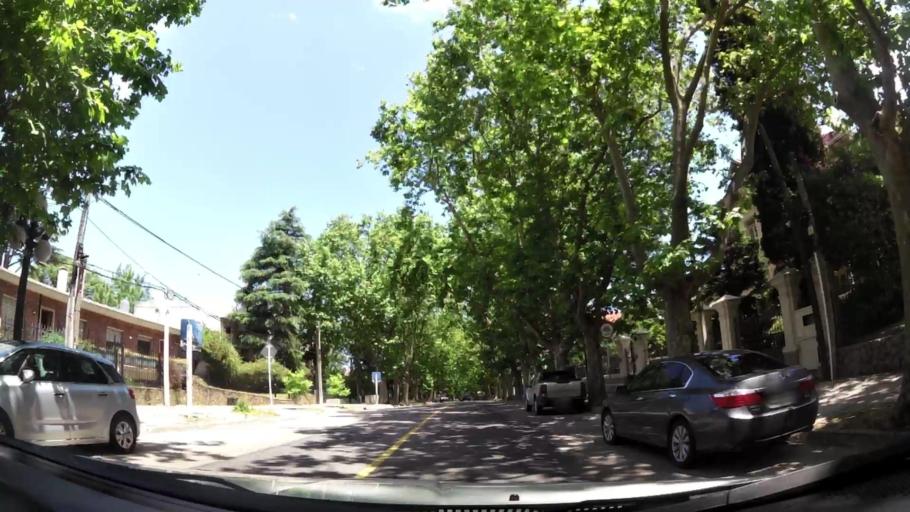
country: UY
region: Montevideo
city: Montevideo
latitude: -34.8643
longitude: -56.2029
